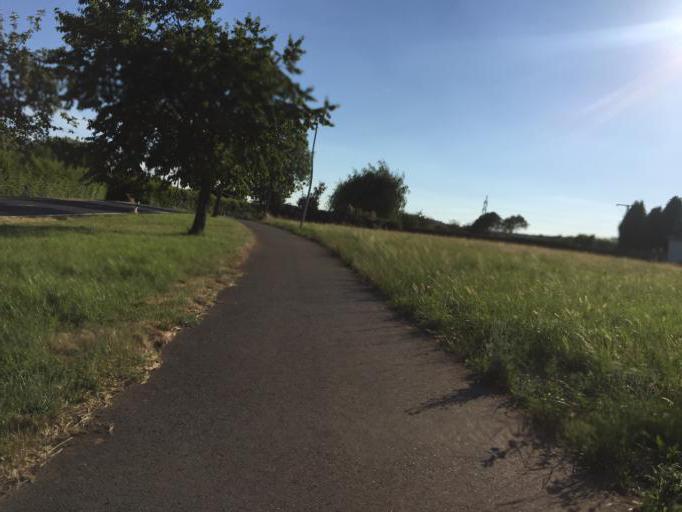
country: DE
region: Rheinland-Pfalz
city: Hartlingen
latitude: 50.5268
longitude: 7.9078
